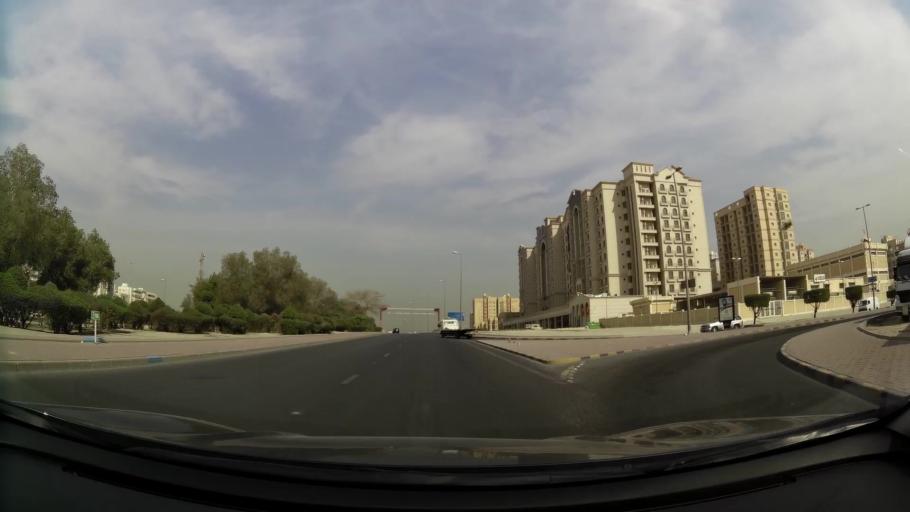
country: KW
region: Al Farwaniyah
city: Janub as Surrah
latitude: 29.2747
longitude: 47.9697
